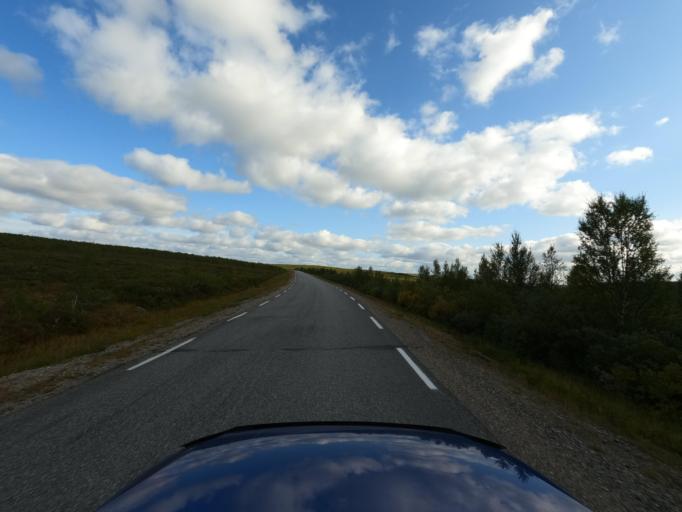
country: NO
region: Finnmark Fylke
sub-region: Porsanger
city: Lakselv
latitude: 69.3742
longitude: 24.4230
